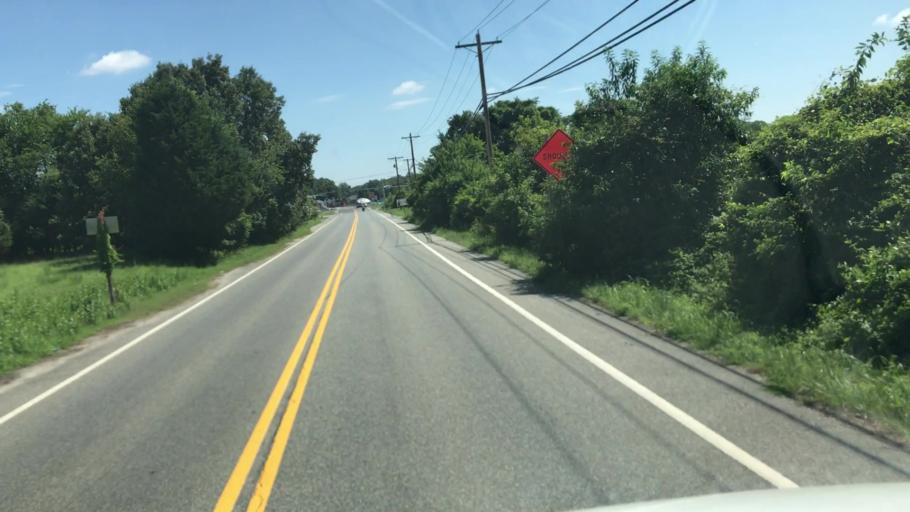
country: US
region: Maryland
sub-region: Prince George's County
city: Brandywine
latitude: 38.7136
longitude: -76.8813
